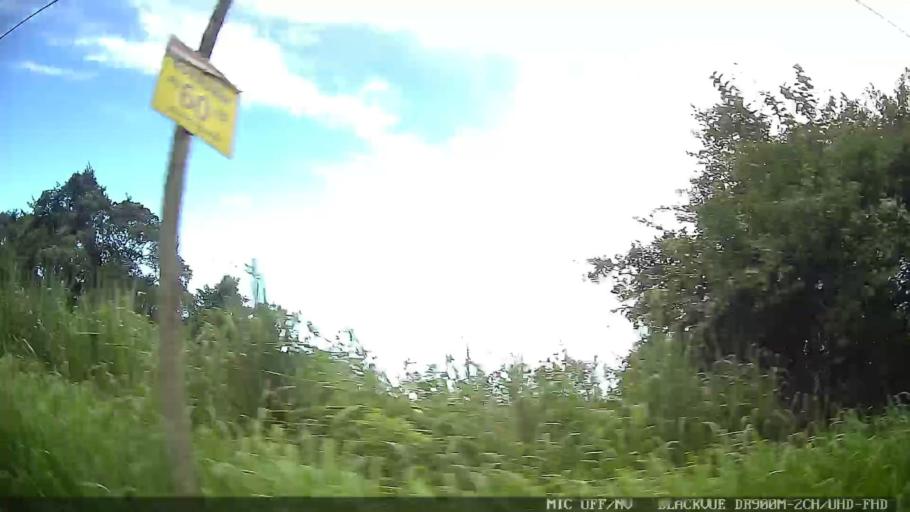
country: BR
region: Sao Paulo
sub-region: Iguape
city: Iguape
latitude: -24.6995
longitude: -47.5359
